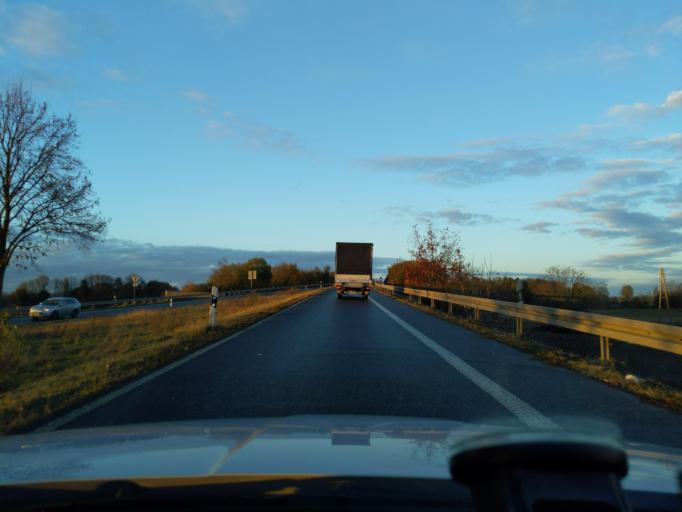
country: DE
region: North Rhine-Westphalia
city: Kalkar
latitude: 51.7087
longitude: 6.3294
